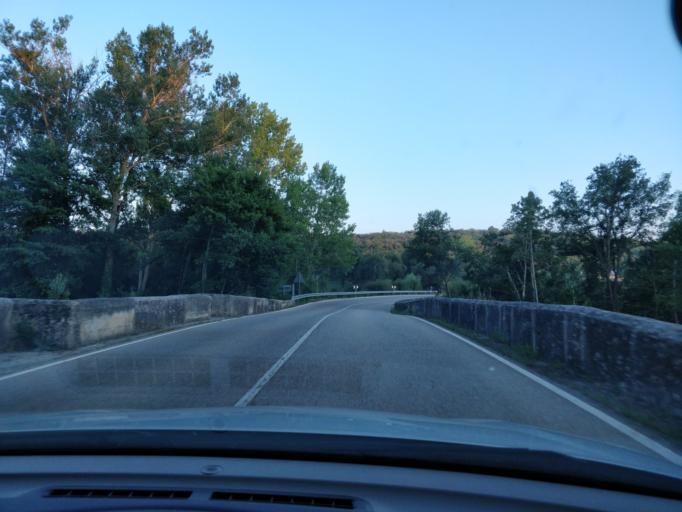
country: ES
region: Castille and Leon
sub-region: Provincia de Burgos
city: Medina de Pomar
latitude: 42.9643
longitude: -3.5478
